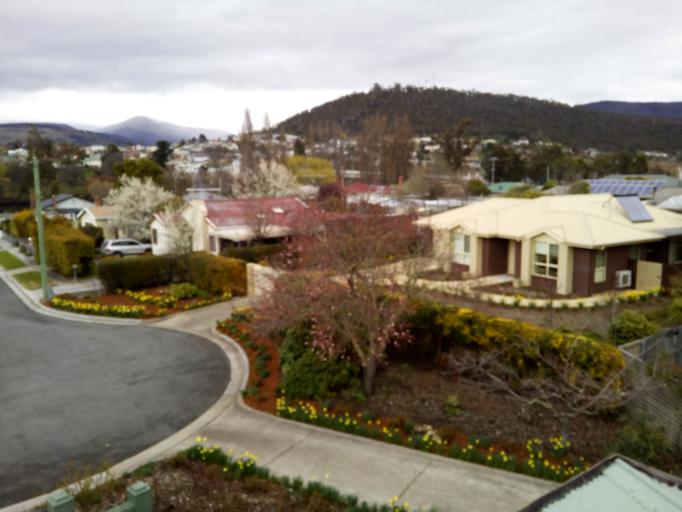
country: AU
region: Tasmania
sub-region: Derwent Valley
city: New Norfolk
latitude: -42.7760
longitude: 147.0577
